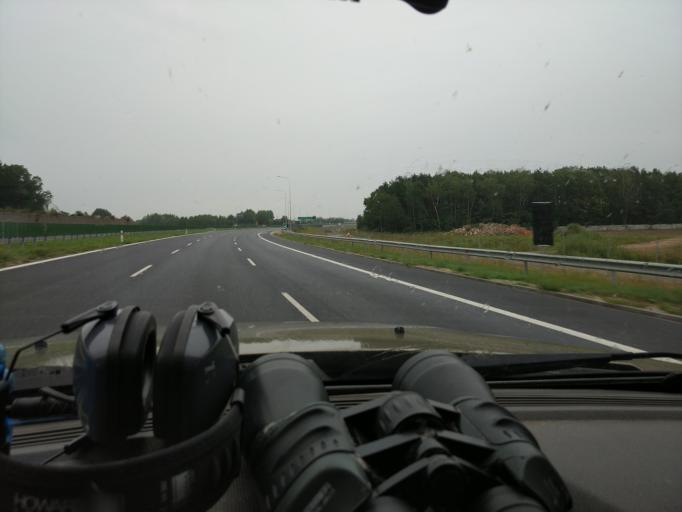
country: PL
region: Masovian Voivodeship
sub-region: Powiat wolominski
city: Slupno
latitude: 52.3475
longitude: 21.1574
